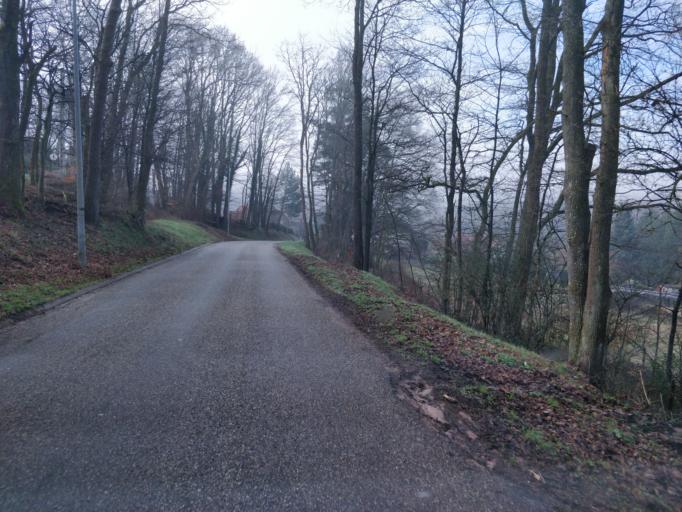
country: FR
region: Lorraine
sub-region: Departement de la Moselle
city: Soucht
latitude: 48.9265
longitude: 7.3687
